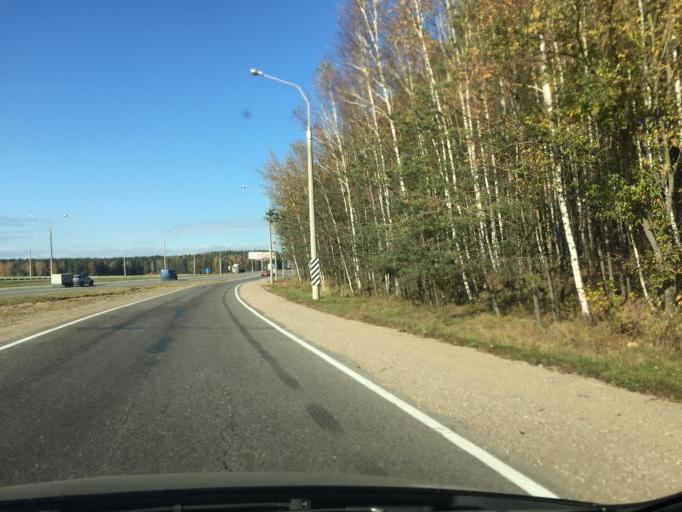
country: BY
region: Minsk
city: Slabada
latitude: 53.9515
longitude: 27.9766
